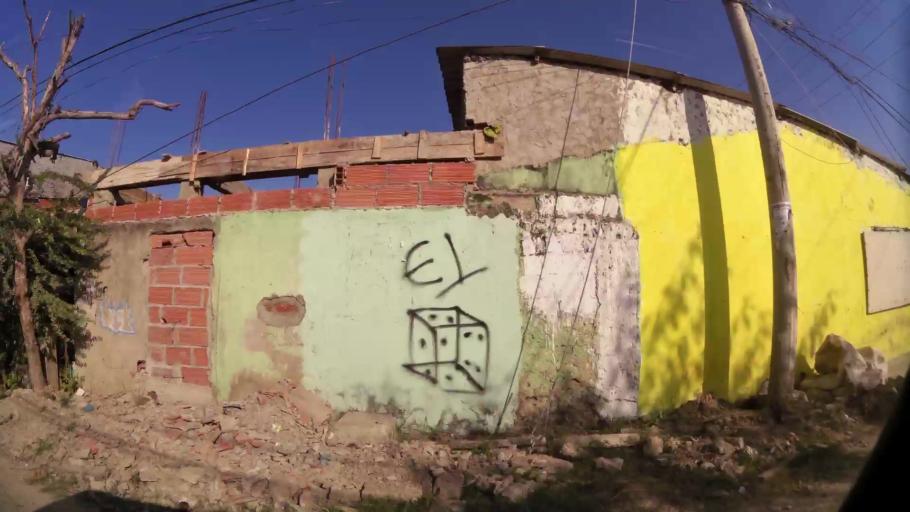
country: CO
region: Bolivar
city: Cartagena
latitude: 10.4099
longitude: -75.4987
